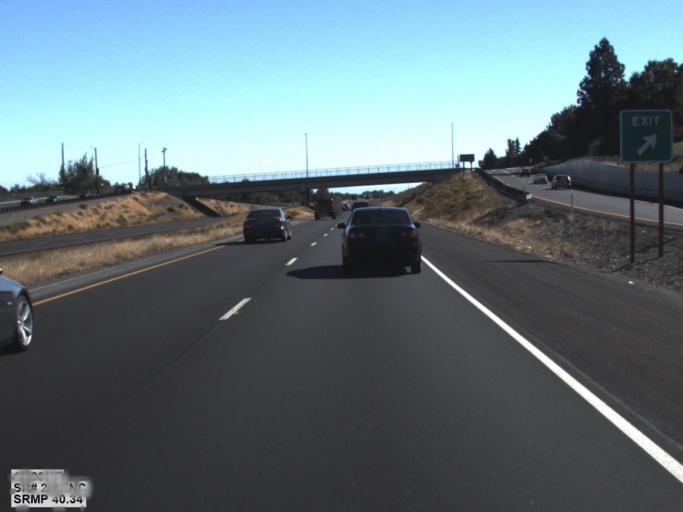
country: US
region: Washington
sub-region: Franklin County
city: West Pasco
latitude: 46.2291
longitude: -119.1940
